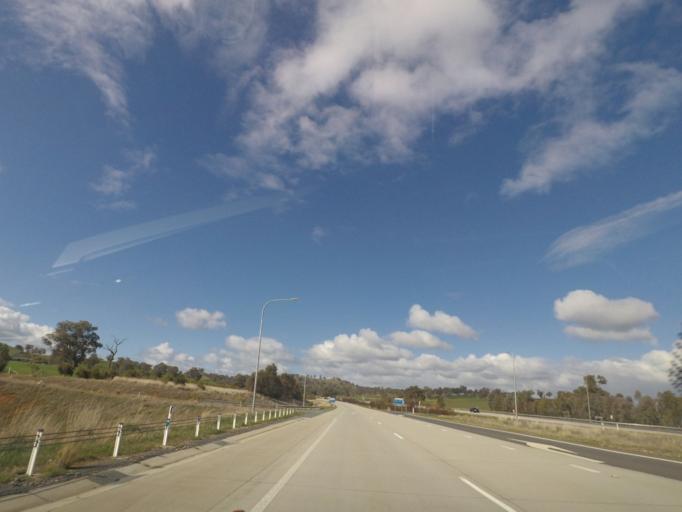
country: AU
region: New South Wales
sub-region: Albury Municipality
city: Lavington
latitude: -35.9266
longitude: 147.0770
